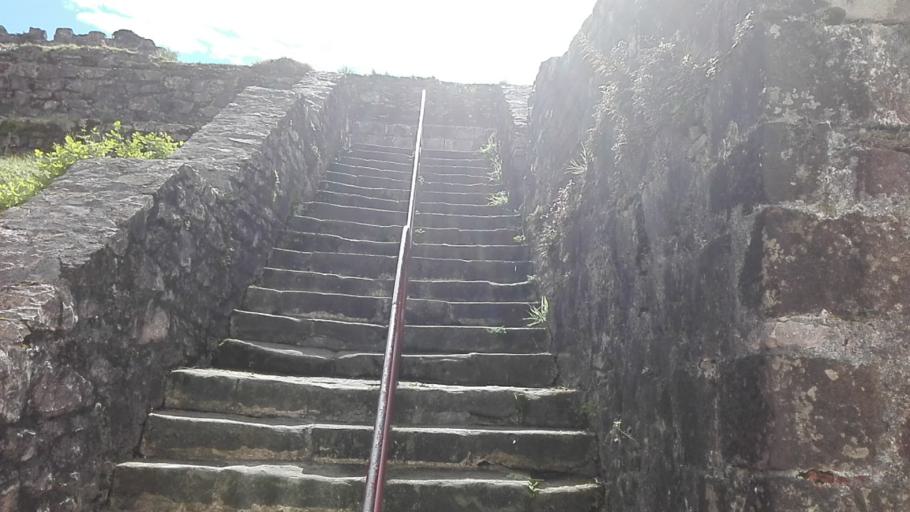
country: ES
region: Basque Country
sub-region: Provincia de Guipuzcoa
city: Fuenterrabia
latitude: 43.3623
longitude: -1.7925
